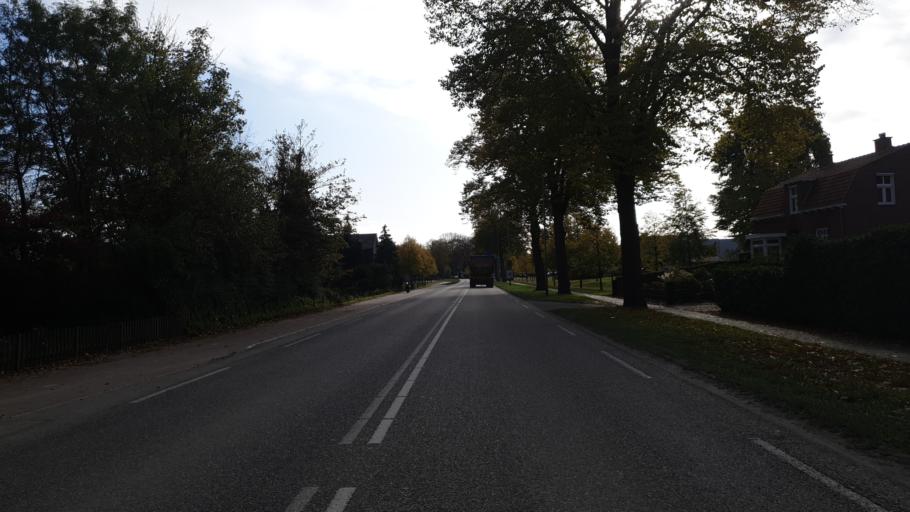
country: NL
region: Limburg
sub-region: Gemeente Gennep
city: Gennep
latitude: 51.6800
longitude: 5.9750
